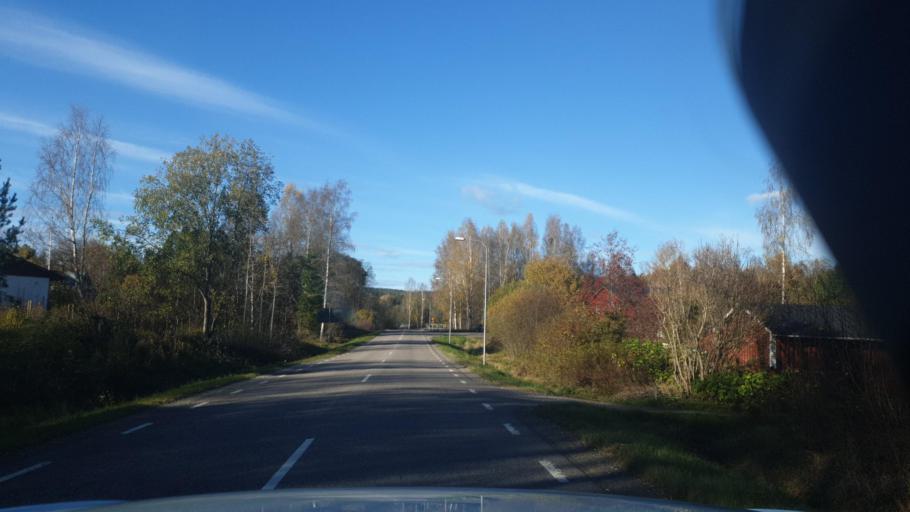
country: SE
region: Vaermland
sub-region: Arvika Kommun
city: Arvika
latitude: 59.6610
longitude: 12.8847
